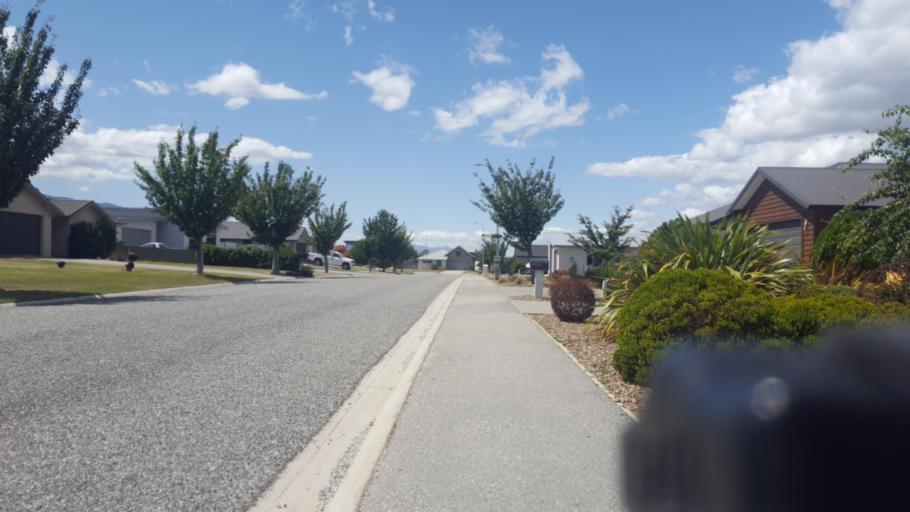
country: NZ
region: Otago
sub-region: Queenstown-Lakes District
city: Wanaka
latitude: -44.9724
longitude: 169.2482
